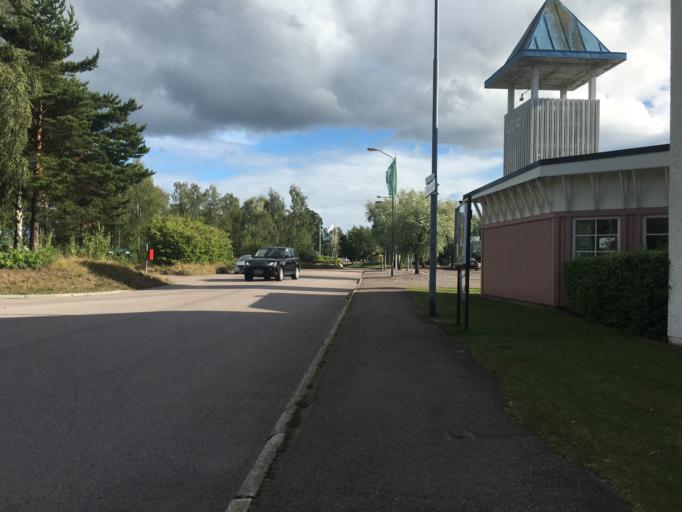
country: SE
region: Kalmar
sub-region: Kalmar Kommun
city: Kalmar
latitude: 56.7036
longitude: 16.3586
